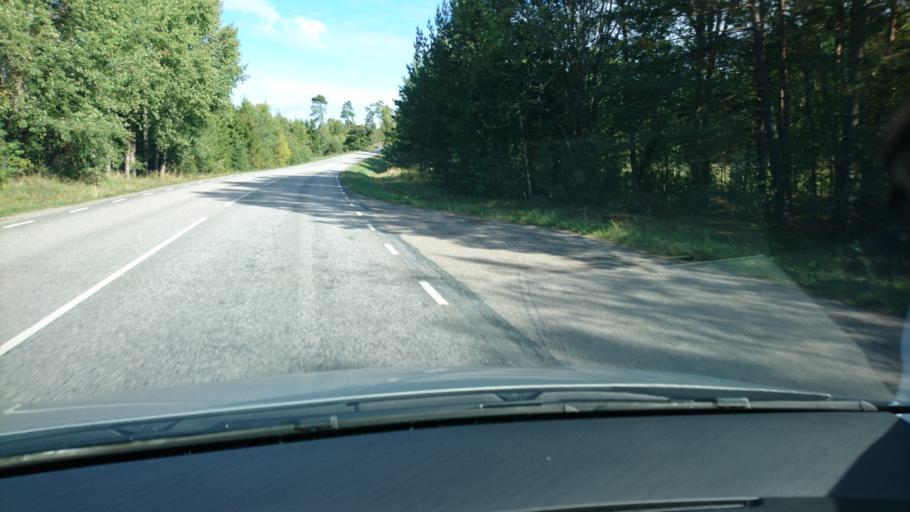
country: SE
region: Soedermanland
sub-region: Strangnas Kommun
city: Stallarholmen
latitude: 59.3423
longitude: 17.1188
